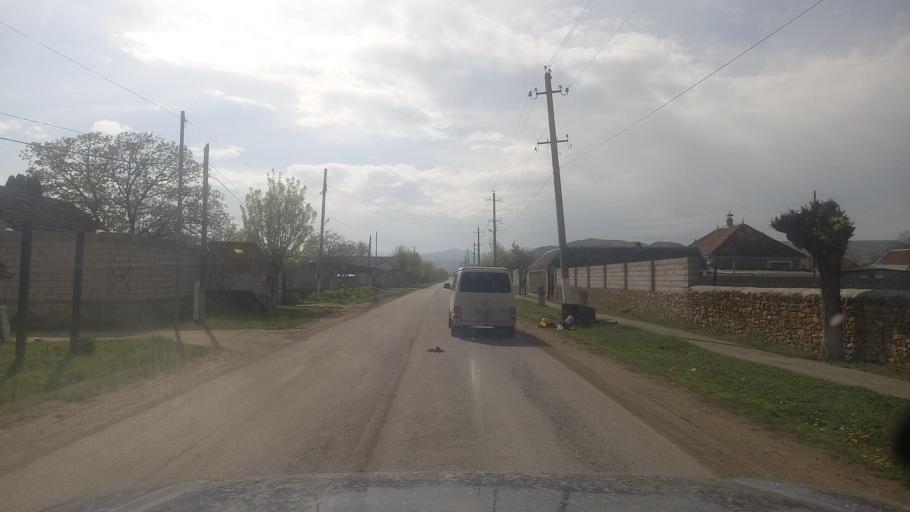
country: RU
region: Kabardino-Balkariya
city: Kamennomostskoye
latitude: 43.7351
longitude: 43.0376
